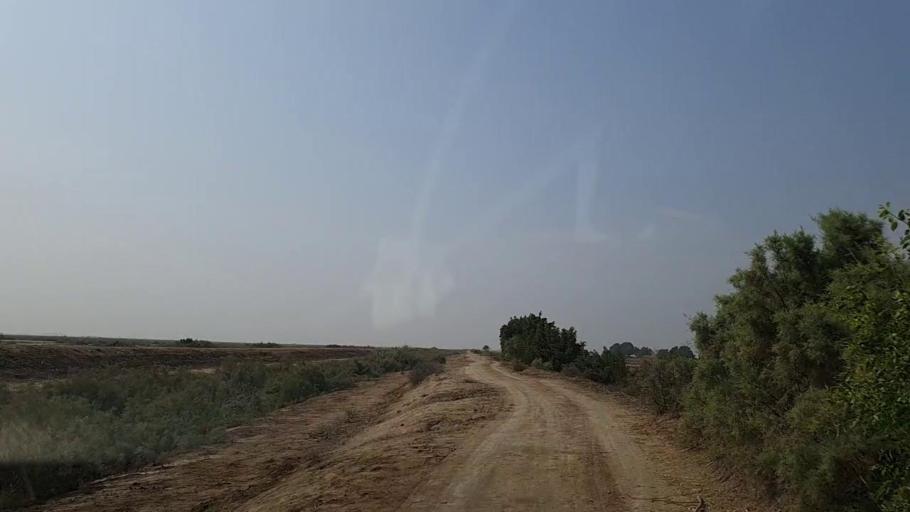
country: PK
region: Sindh
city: Gharo
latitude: 24.6738
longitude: 67.7261
